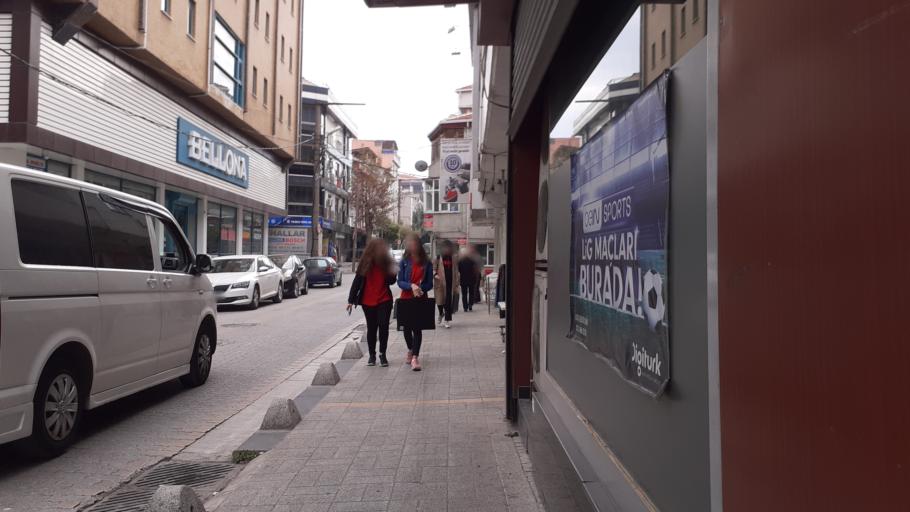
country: TR
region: Istanbul
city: Mahmutbey
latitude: 40.9922
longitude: 28.7854
